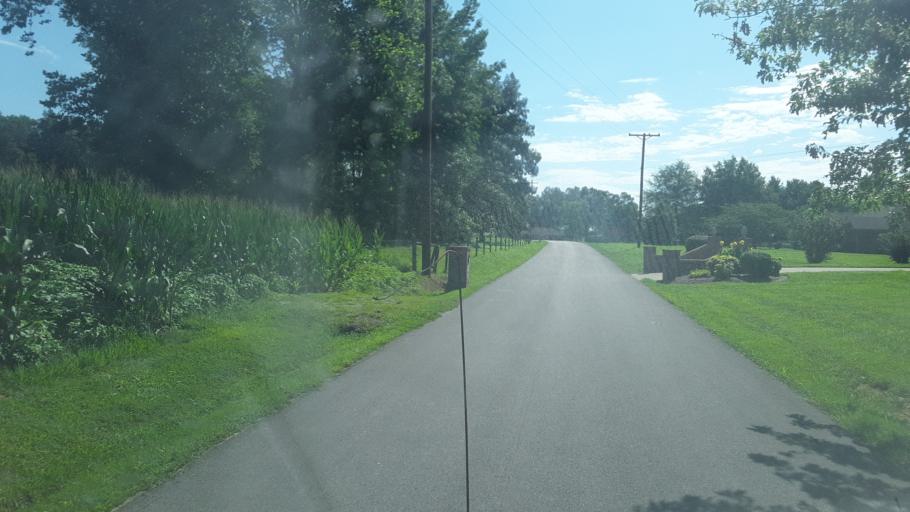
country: US
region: Kentucky
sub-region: Todd County
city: Elkton
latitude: 36.7961
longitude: -87.2003
